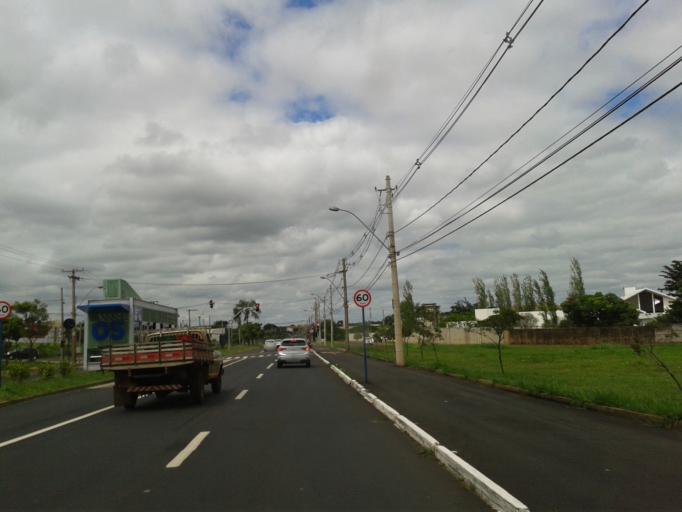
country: BR
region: Minas Gerais
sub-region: Uberaba
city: Uberaba
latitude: -19.7460
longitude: -47.9657
